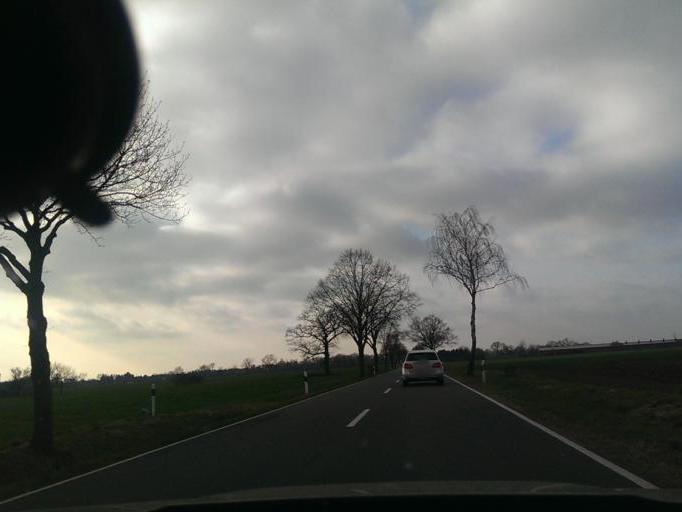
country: DE
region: Lower Saxony
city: Elze
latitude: 52.5717
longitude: 9.7524
